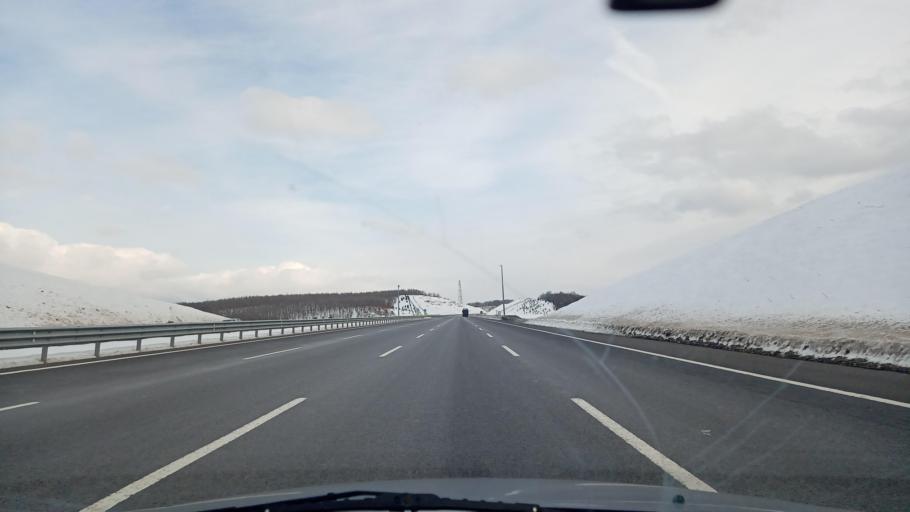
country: TR
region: Kocaeli
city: Hereke
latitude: 40.8970
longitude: 29.6314
